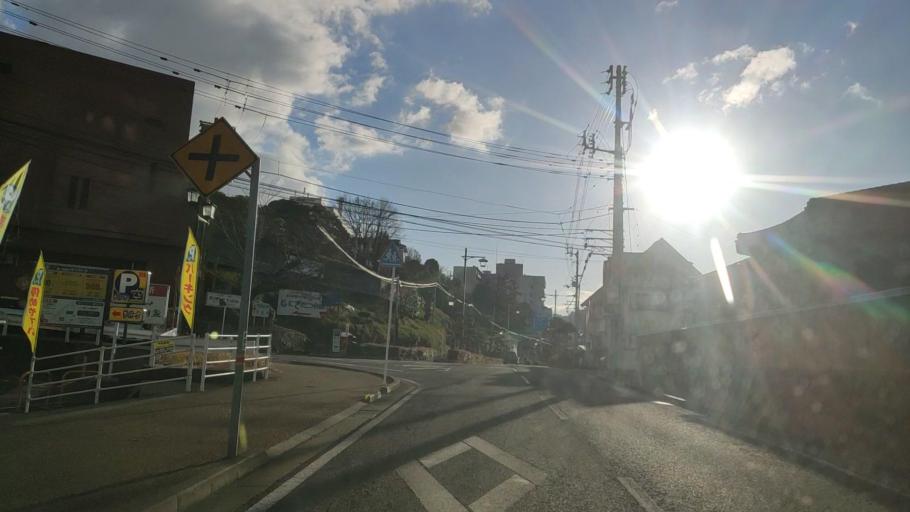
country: JP
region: Ehime
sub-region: Shikoku-chuo Shi
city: Matsuyama
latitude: 33.8497
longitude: 132.7878
